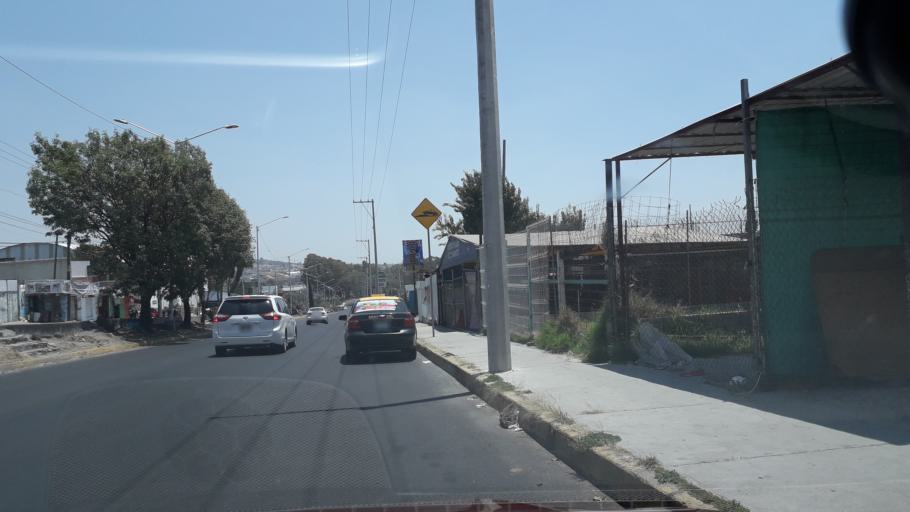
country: MX
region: Puebla
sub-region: Puebla
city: Galaxia la Calera
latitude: 18.9944
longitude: -98.1789
